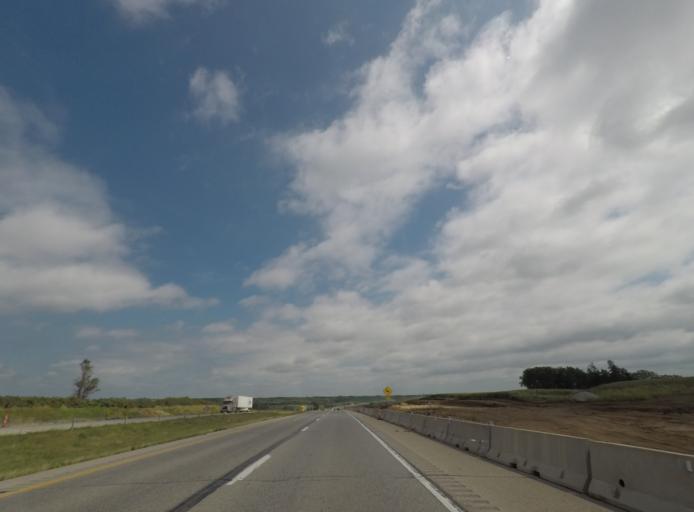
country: US
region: Iowa
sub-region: Poweshiek County
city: Grinnell
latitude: 41.6889
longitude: -92.8762
